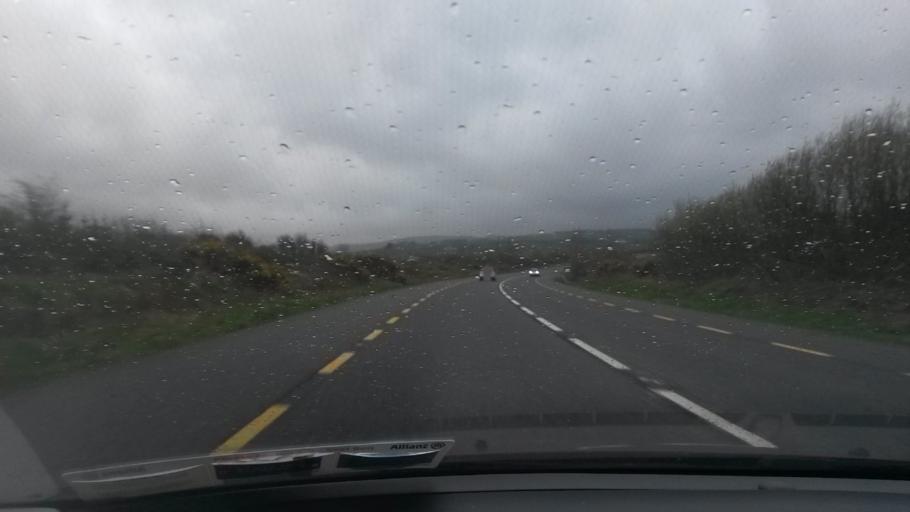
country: IE
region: Munster
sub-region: County Limerick
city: Abbeyfeale
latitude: 52.3159
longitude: -9.3599
